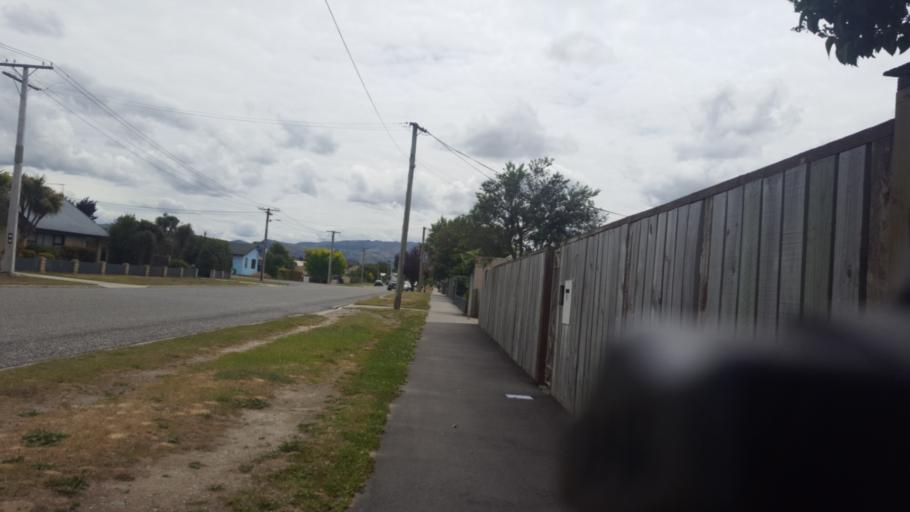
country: NZ
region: Otago
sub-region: Queenstown-Lakes District
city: Wanaka
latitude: -45.2510
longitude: 169.3834
